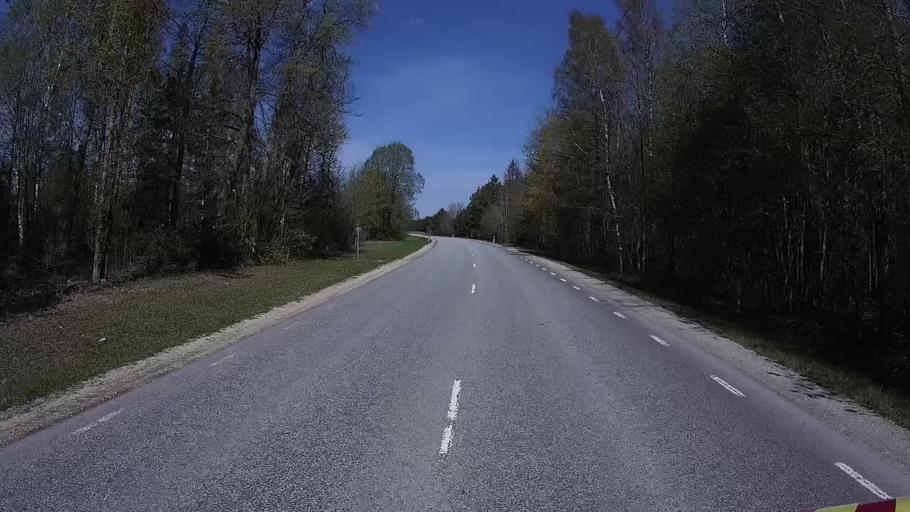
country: EE
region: Harju
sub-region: Keila linn
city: Keila
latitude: 59.2614
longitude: 24.2911
